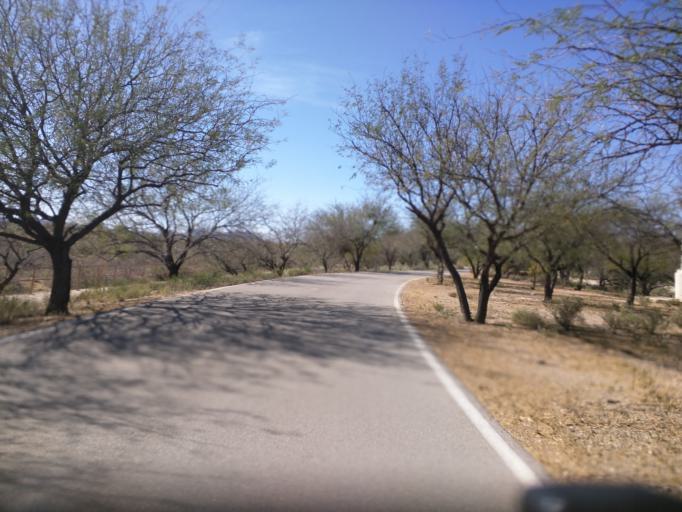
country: US
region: Arizona
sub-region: Pima County
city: Flowing Wells
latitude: 32.2989
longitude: -111.0045
